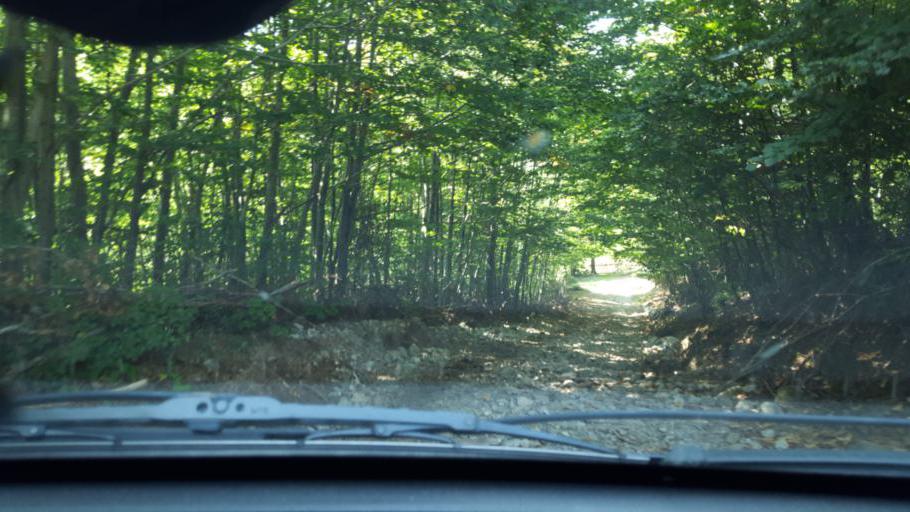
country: ME
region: Andrijevica
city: Andrijevica
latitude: 42.5880
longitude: 19.6371
